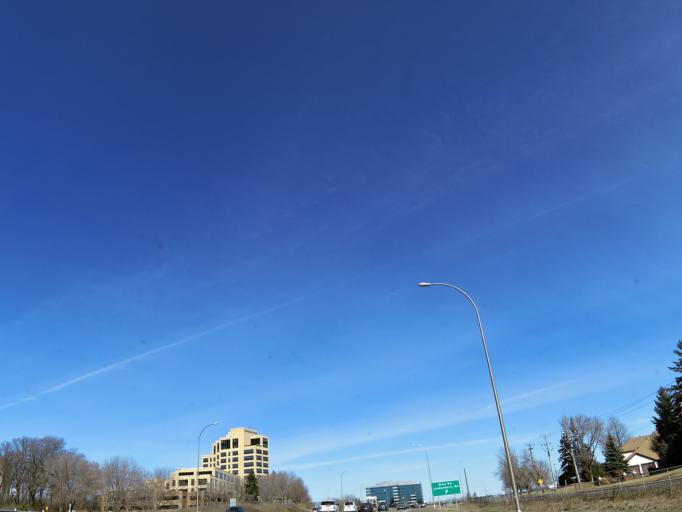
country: US
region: Minnesota
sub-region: Hennepin County
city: Edina
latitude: 44.8946
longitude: -93.4005
